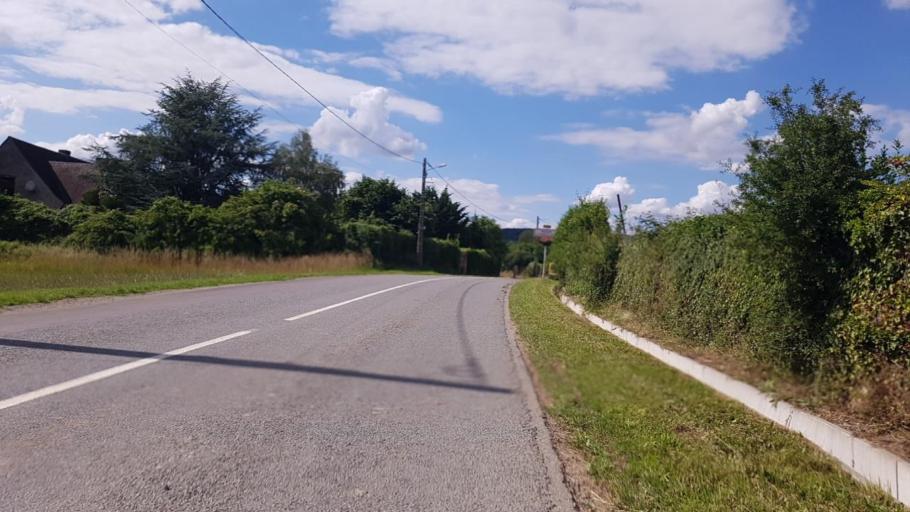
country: FR
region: Picardie
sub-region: Departement de l'Aisne
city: Crezancy
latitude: 49.0714
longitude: 3.5646
